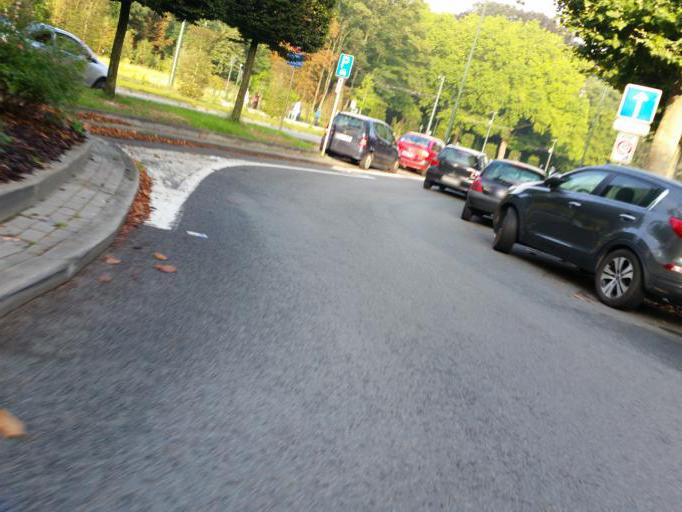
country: BE
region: Flanders
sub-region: Provincie Vlaams-Brabant
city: Grimbergen
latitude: 50.8929
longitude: 4.3648
